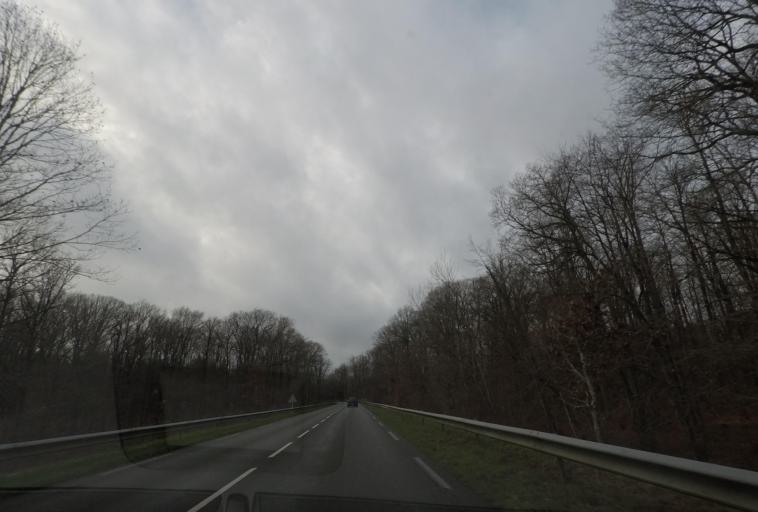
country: FR
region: Pays de la Loire
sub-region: Departement de la Sarthe
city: Vibraye
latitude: 48.0417
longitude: 0.7453
